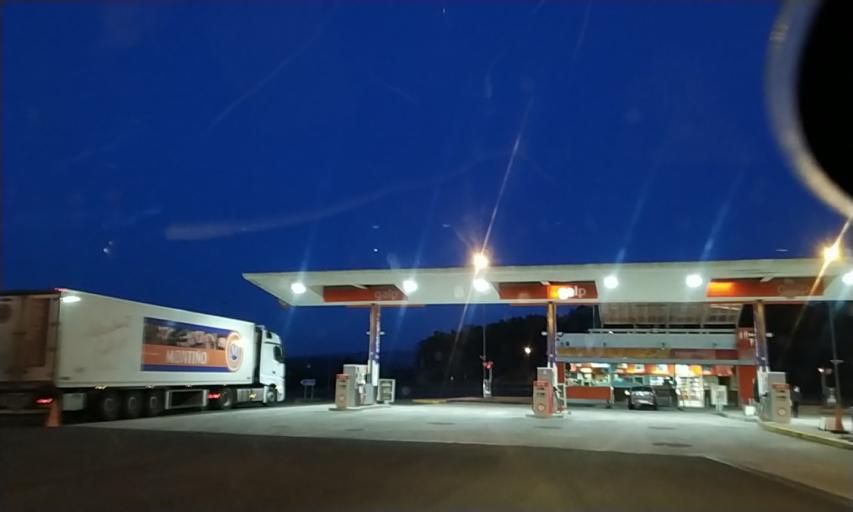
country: ES
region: Galicia
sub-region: Provincia de Pontevedra
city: Silleda
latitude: 42.7165
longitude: -8.3016
